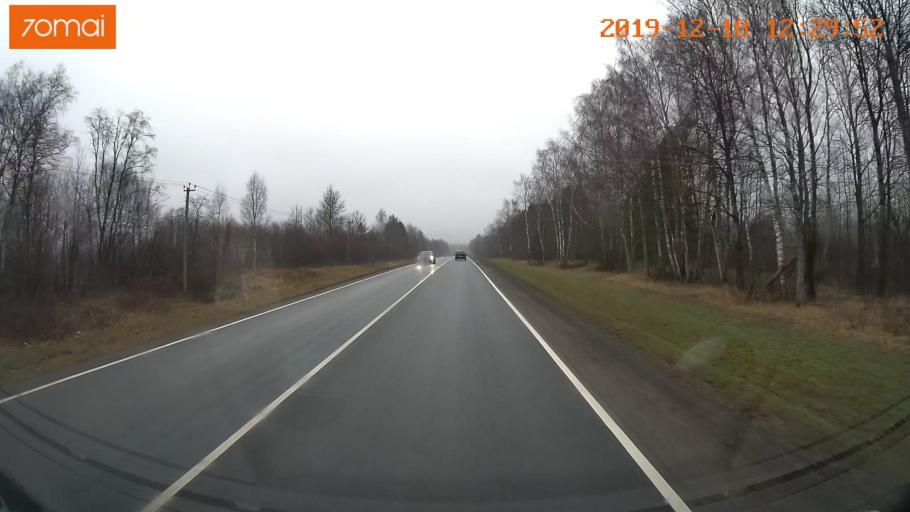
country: RU
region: Moskovskaya
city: Novopetrovskoye
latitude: 56.0829
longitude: 36.5206
